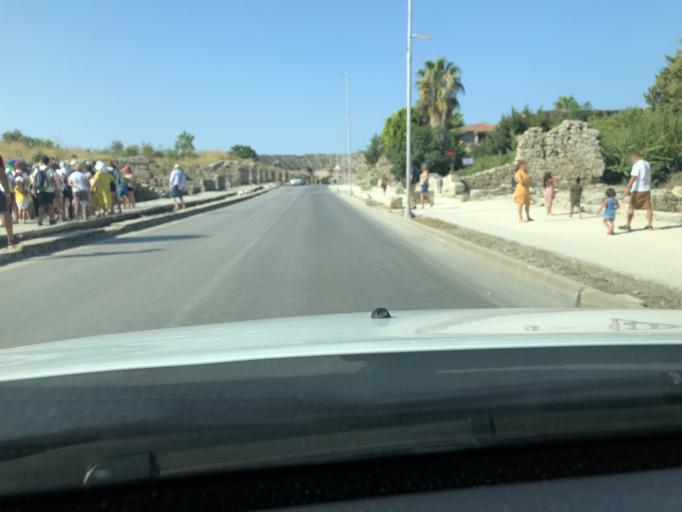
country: TR
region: Antalya
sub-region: Manavgat
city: Side
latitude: 36.7701
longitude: 31.3930
